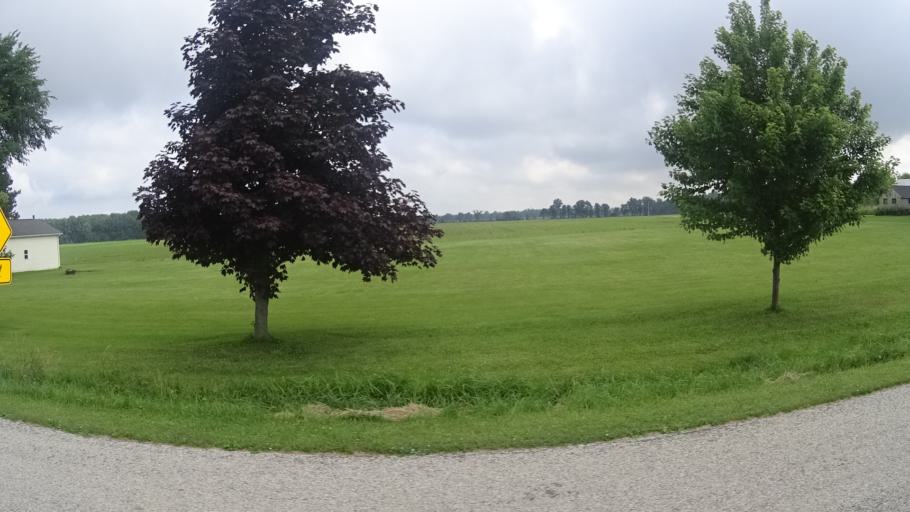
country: US
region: Ohio
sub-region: Huron County
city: Wakeman
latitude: 41.2843
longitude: -82.4638
